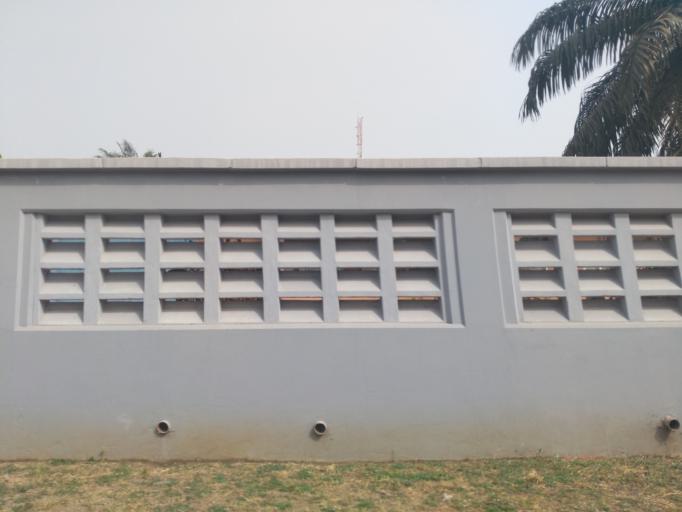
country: GH
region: Ashanti
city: Kumasi
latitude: 6.6787
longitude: -1.6062
